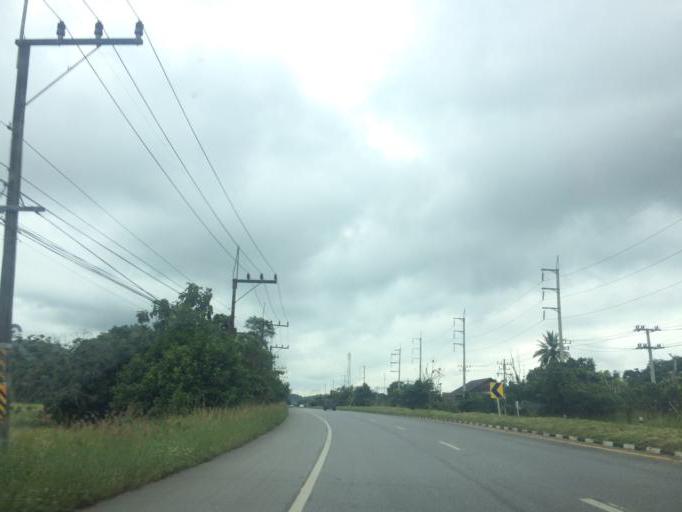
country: TH
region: Chiang Rai
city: Mae Chan
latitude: 20.0901
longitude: 99.8749
